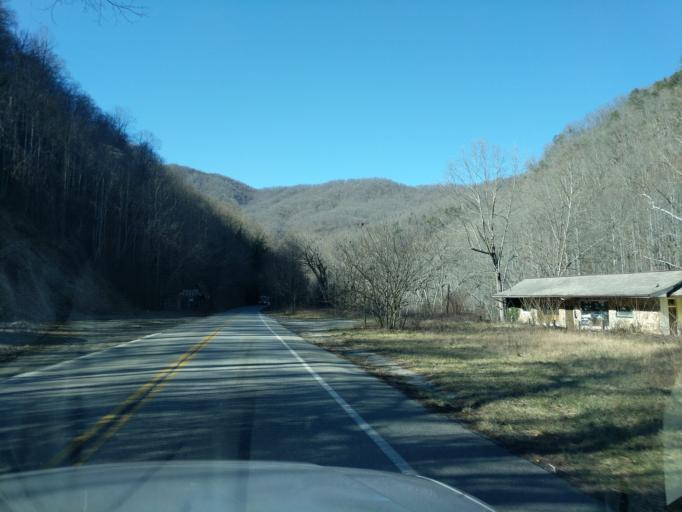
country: US
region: North Carolina
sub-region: Swain County
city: Bryson City
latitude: 35.3324
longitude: -83.6095
